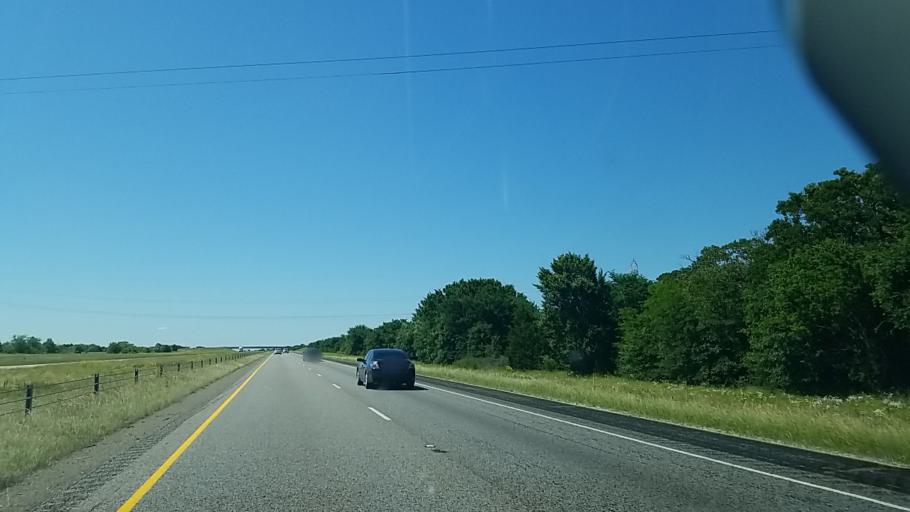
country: US
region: Texas
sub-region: Freestone County
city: Fairfield
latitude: 31.8224
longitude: -96.2791
